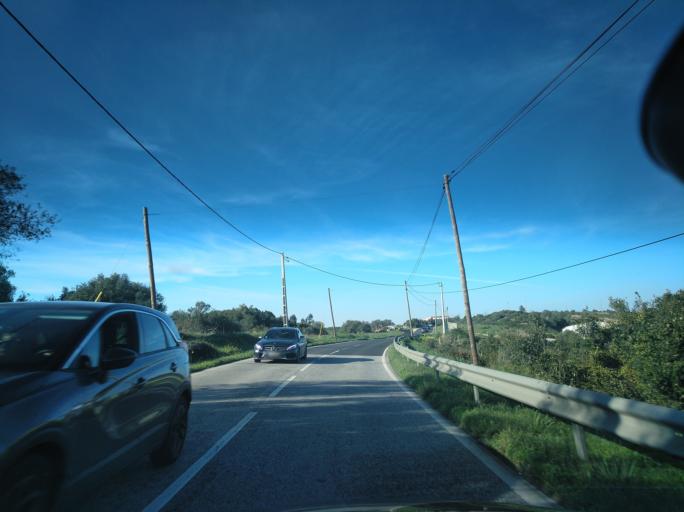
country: PT
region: Lisbon
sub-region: Mafra
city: Mafra
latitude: 38.9017
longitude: -9.3275
